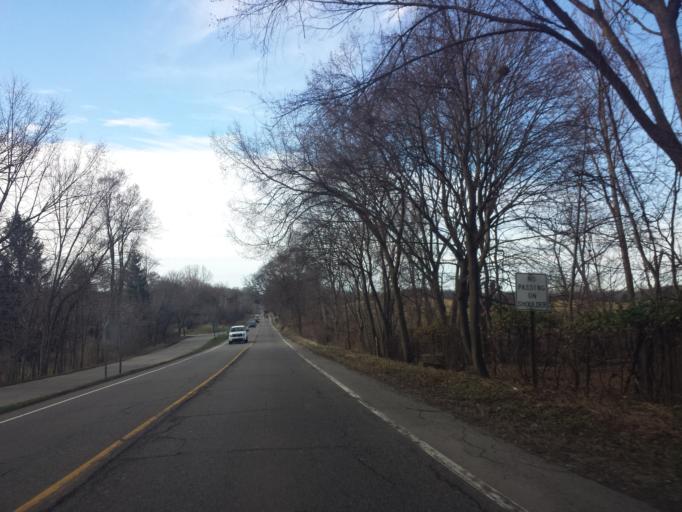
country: US
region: Michigan
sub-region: Oakland County
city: Auburn Hills
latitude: 42.6719
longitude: -83.1937
